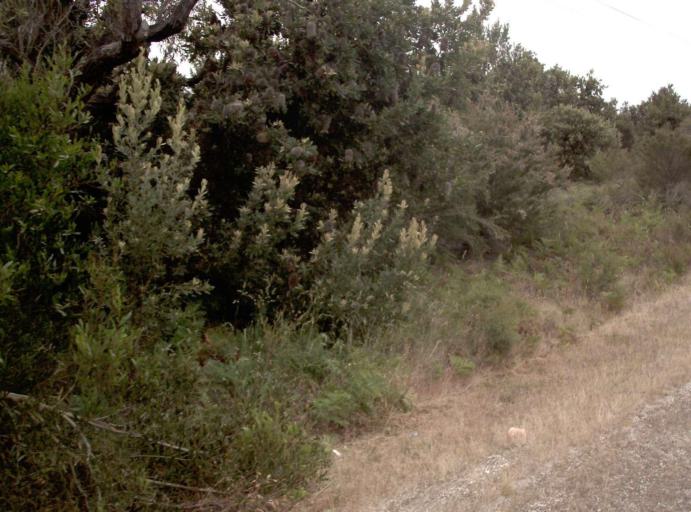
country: AU
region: Victoria
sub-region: Wellington
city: Sale
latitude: -38.1990
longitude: 147.3522
